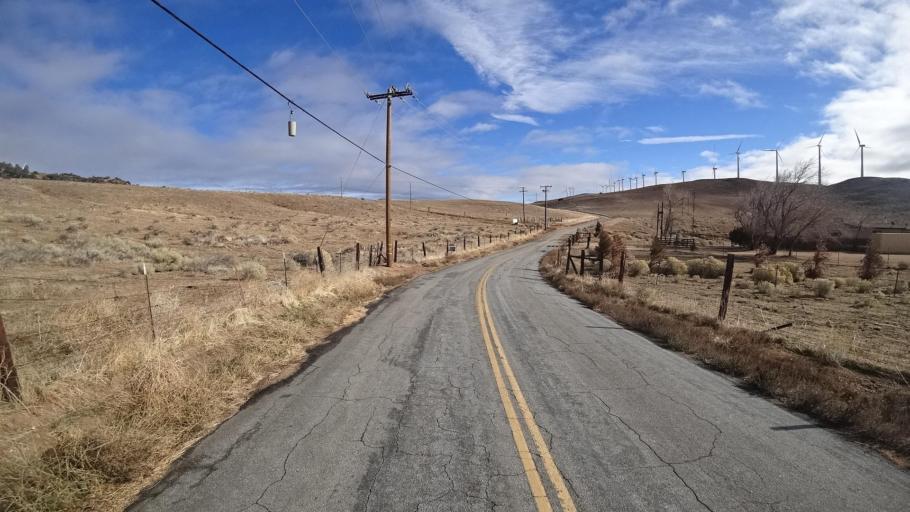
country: US
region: California
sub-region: Kern County
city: Tehachapi
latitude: 35.0699
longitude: -118.3468
